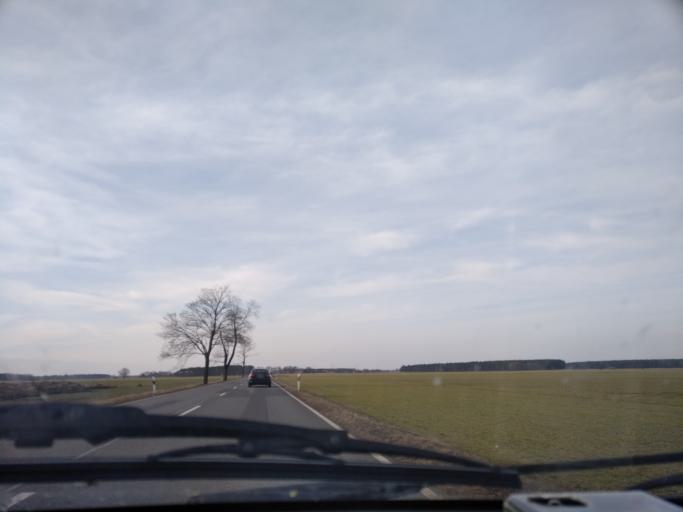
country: DE
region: Saxony-Anhalt
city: Holzdorf
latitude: 51.7870
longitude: 13.1894
